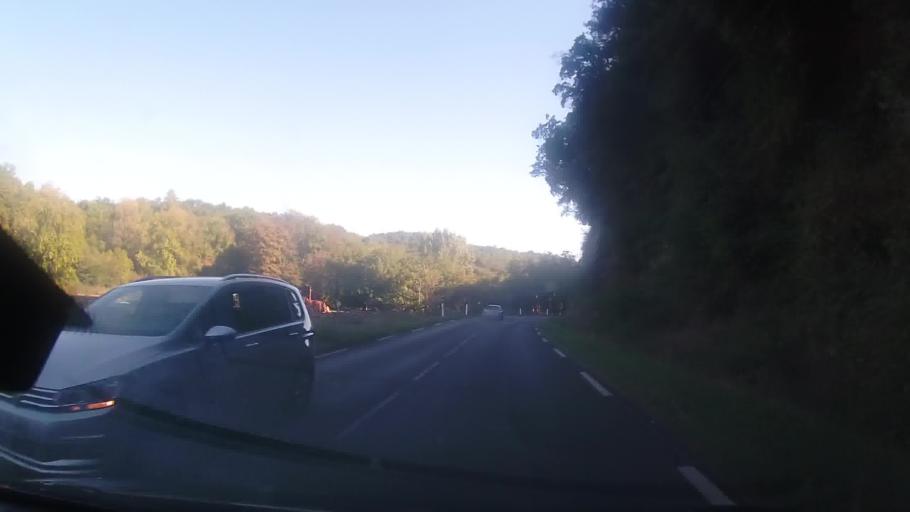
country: FR
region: Aquitaine
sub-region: Departement de la Dordogne
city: Sarlat-la-Caneda
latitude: 44.8541
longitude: 1.2141
